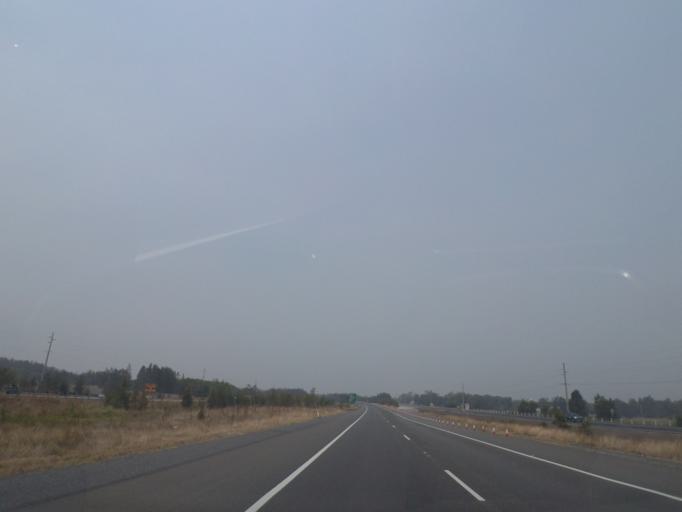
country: AU
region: New South Wales
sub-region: Ballina
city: Ballina
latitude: -28.8652
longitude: 153.5046
